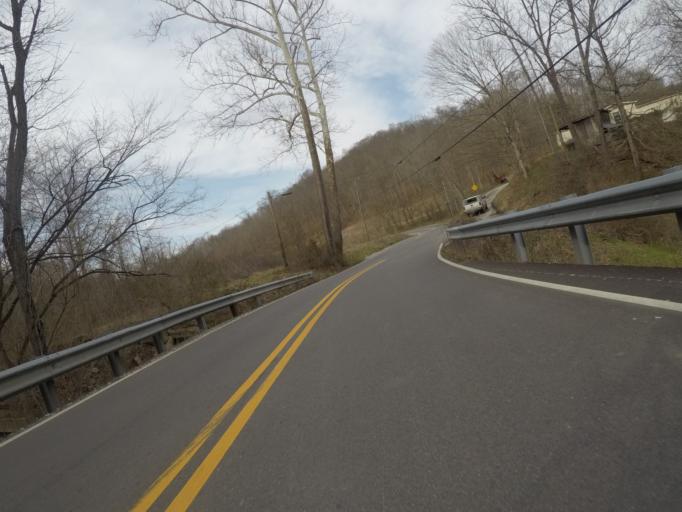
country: US
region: Ohio
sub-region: Lawrence County
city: Burlington
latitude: 38.4324
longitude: -82.4939
